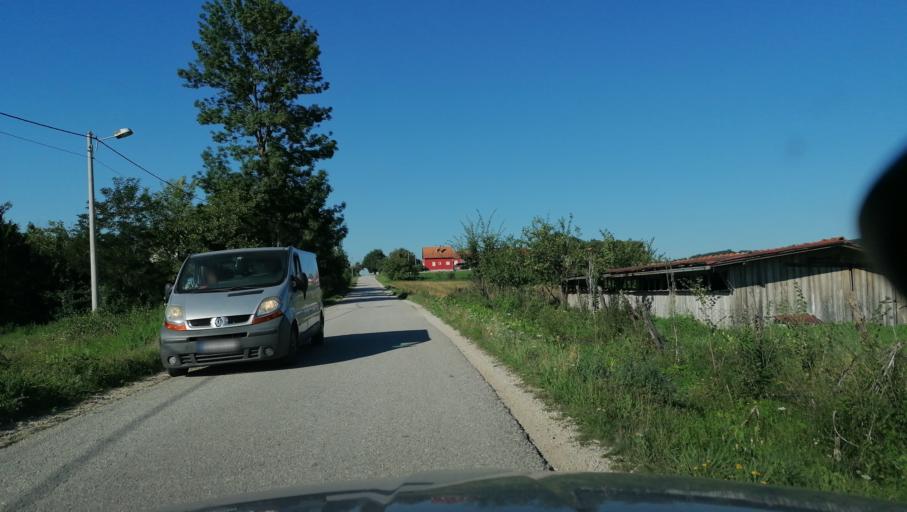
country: RS
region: Central Serbia
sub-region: Sumadijski Okrug
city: Knic
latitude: 43.8712
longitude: 20.6084
